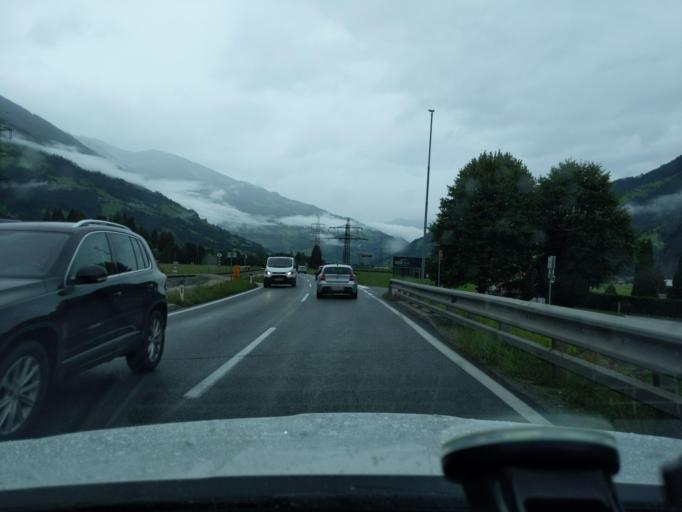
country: AT
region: Tyrol
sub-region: Politischer Bezirk Schwaz
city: Mayrhofen
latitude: 47.1754
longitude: 11.8656
